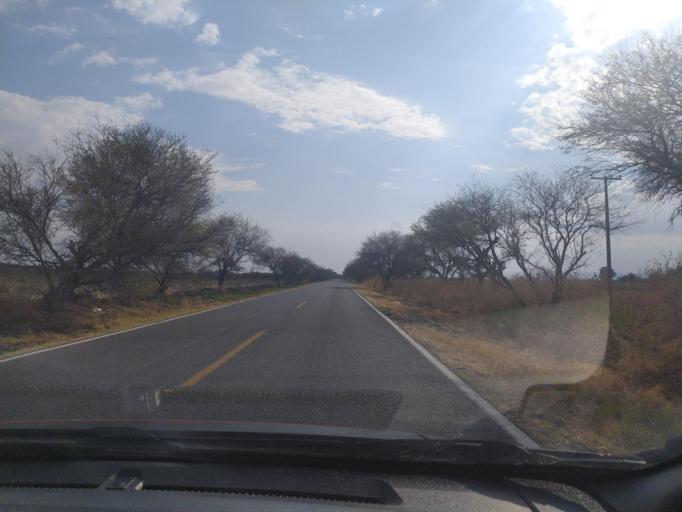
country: MX
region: Guanajuato
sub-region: San Francisco del Rincon
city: San Ignacio de Hidalgo
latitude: 20.9265
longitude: -101.8526
